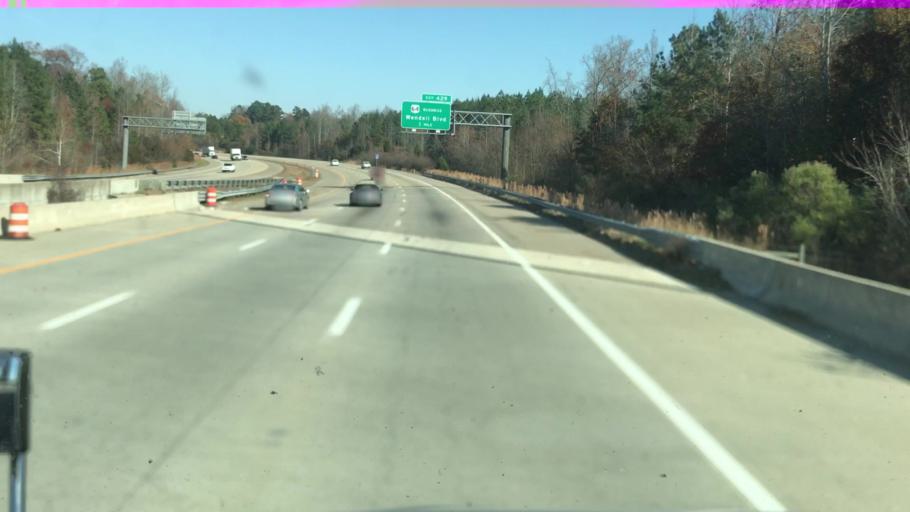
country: US
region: North Carolina
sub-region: Wake County
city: Knightdale
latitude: 35.7856
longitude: -78.4364
